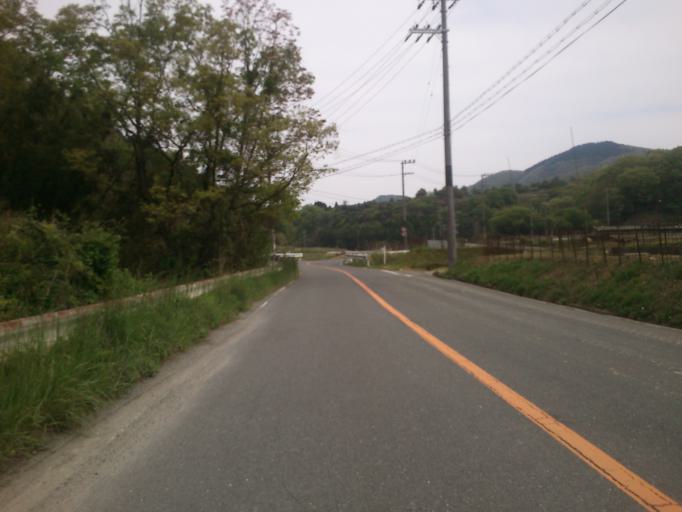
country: JP
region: Kyoto
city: Kameoka
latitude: 34.9648
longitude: 135.4940
